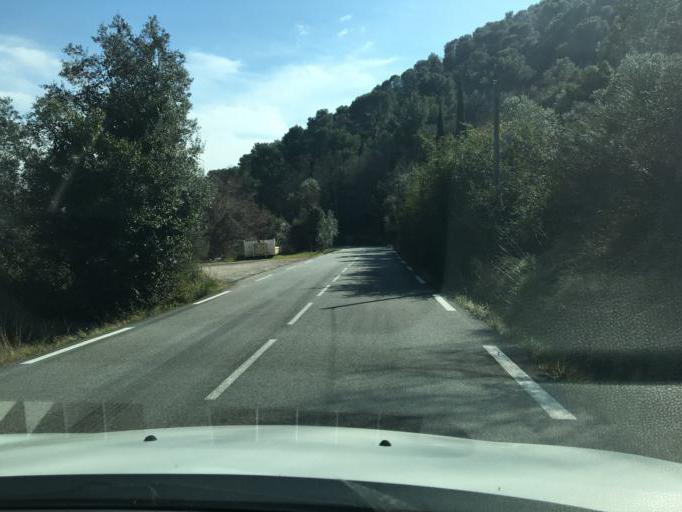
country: FR
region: Provence-Alpes-Cote d'Azur
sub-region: Departement du Var
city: Bargemon
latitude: 43.6135
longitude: 6.5458
